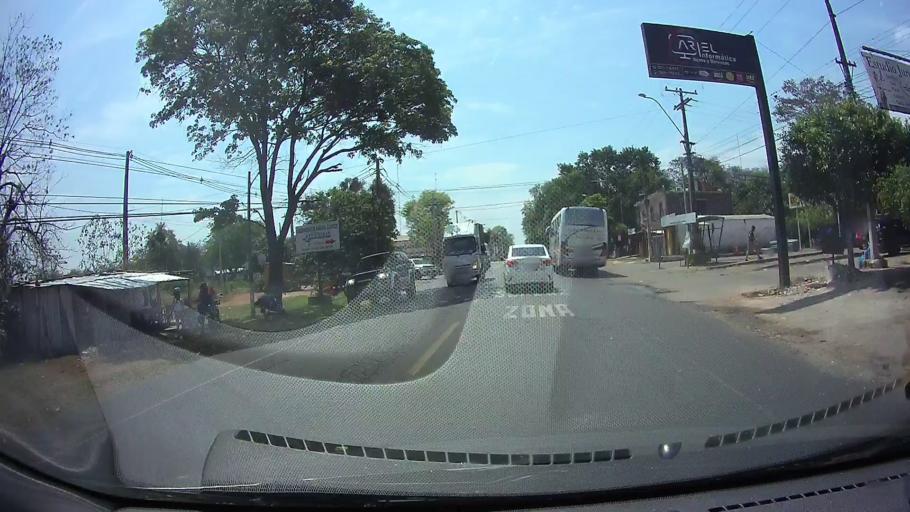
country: PY
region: Central
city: Capiata
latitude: -25.3846
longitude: -57.4725
